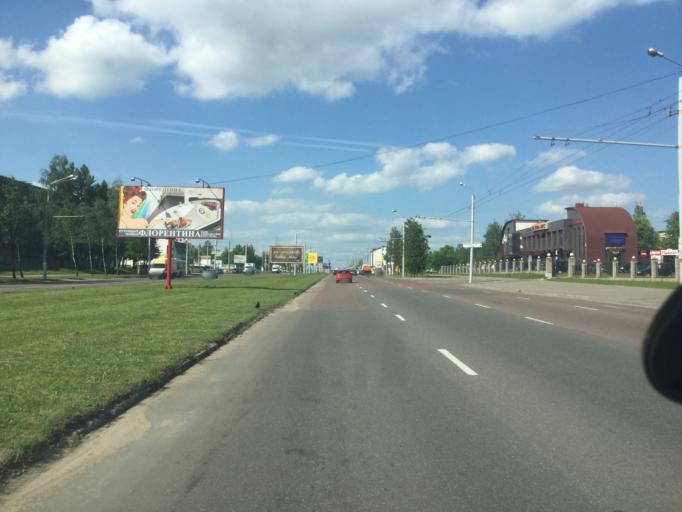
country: BY
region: Vitebsk
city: Vitebsk
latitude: 55.1790
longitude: 30.2462
